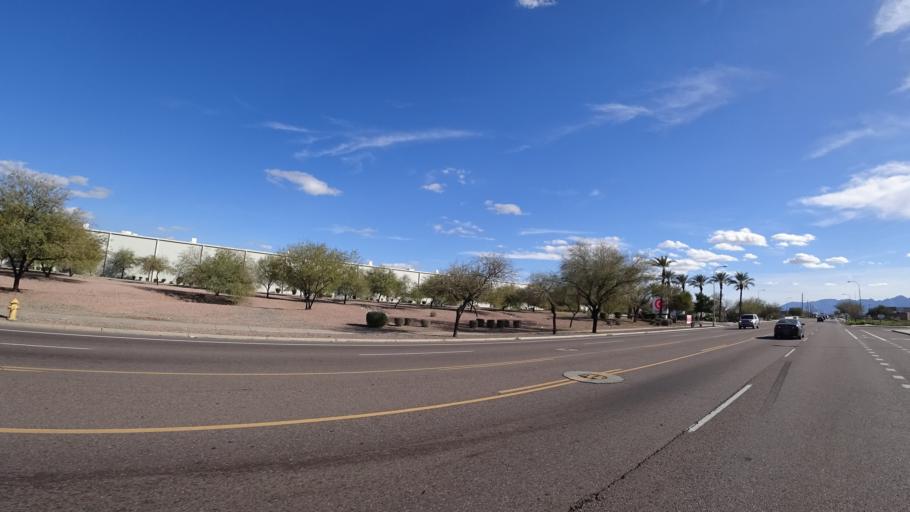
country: US
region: Arizona
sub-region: Maricopa County
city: Tolleson
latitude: 33.4475
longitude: -112.2212
